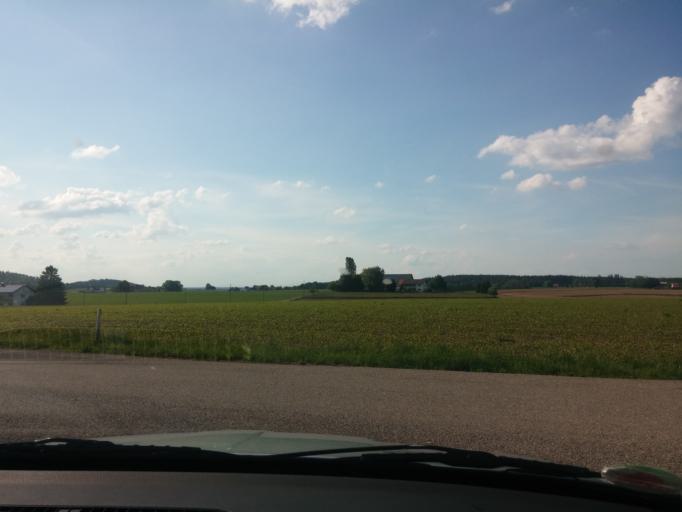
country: DE
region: Bavaria
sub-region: Swabia
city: Woringen
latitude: 47.8869
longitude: 10.1973
